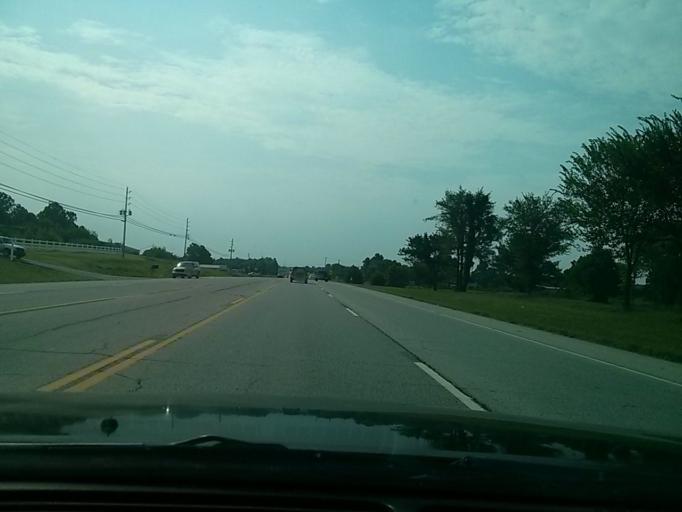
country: US
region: Oklahoma
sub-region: Wagoner County
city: Coweta
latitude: 35.9770
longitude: -95.6638
